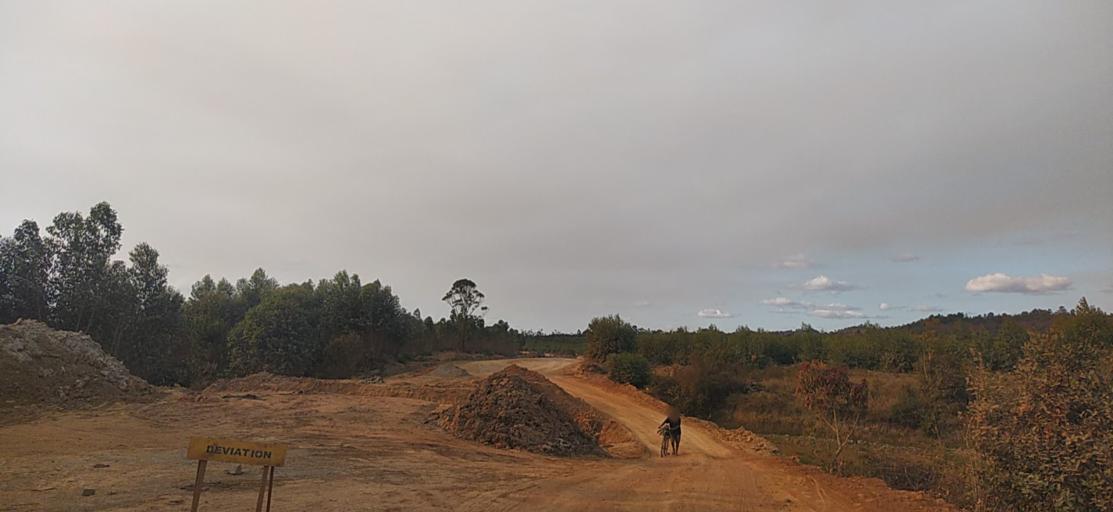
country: MG
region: Alaotra Mangoro
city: Moramanga
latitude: -18.5955
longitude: 48.2775
